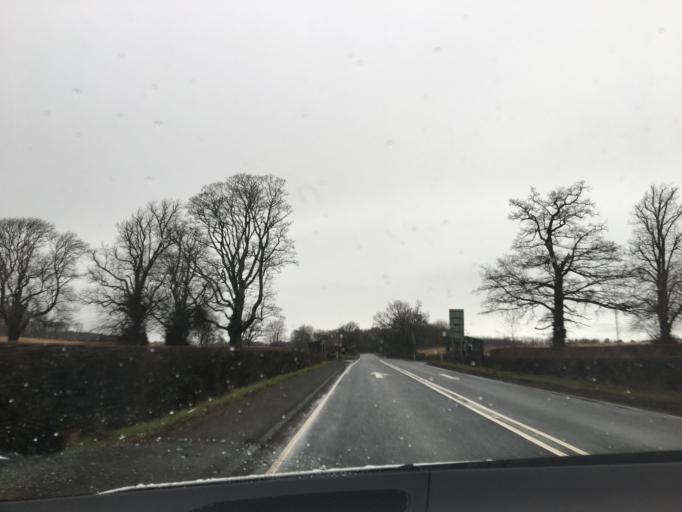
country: GB
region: Scotland
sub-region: Stirling
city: Doune
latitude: 56.1657
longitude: -4.0641
